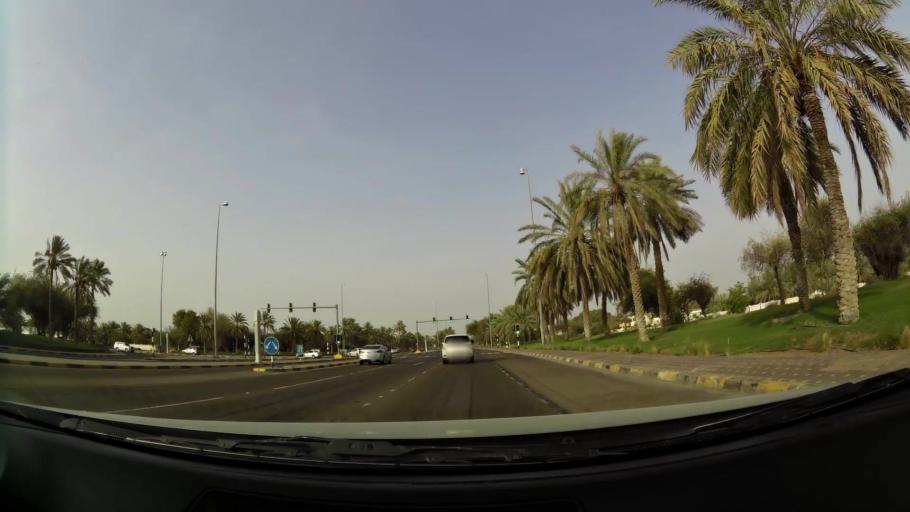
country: AE
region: Abu Dhabi
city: Al Ain
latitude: 24.2215
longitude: 55.6965
